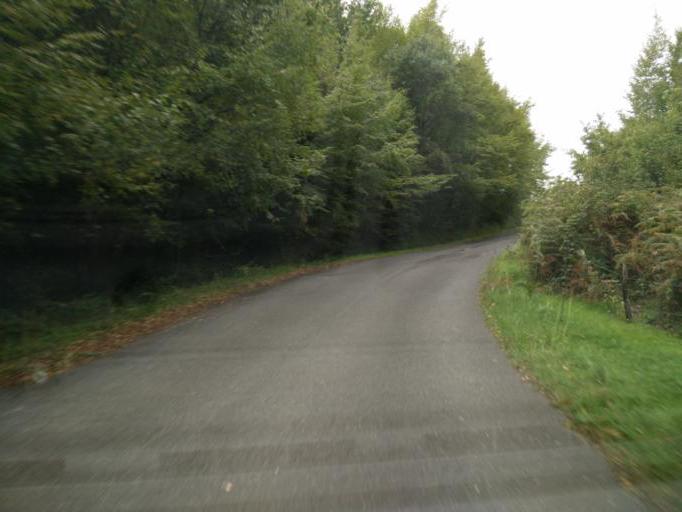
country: IT
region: Tuscany
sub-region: Provincia di Massa-Carrara
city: Licciana Nardi
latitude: 44.2834
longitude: 10.0274
